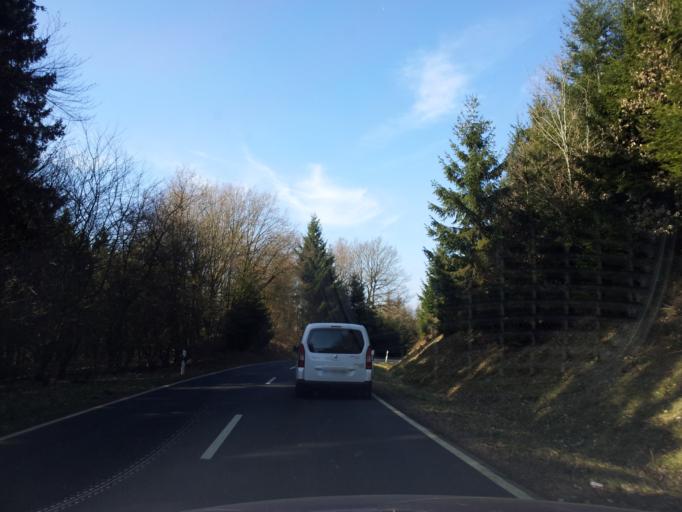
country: DE
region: Rheinland-Pfalz
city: Grosslangenfeld
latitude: 50.2110
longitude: 6.2554
